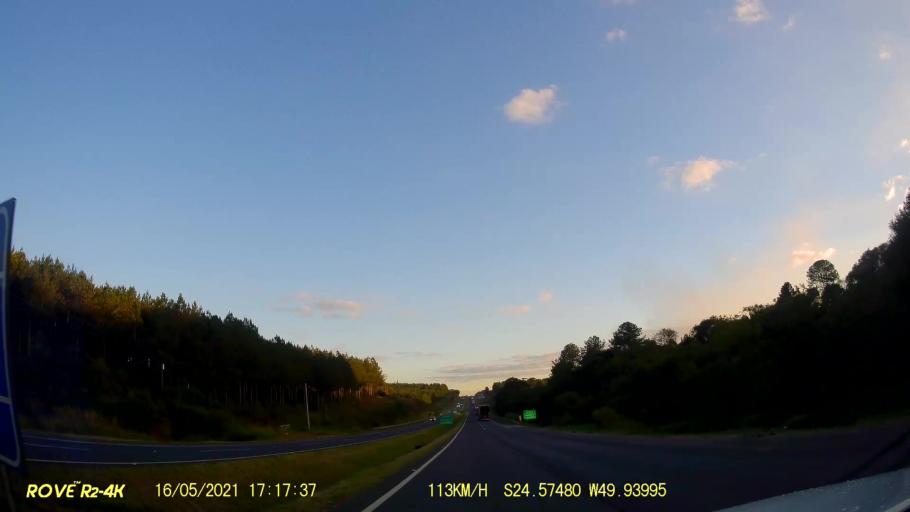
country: BR
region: Parana
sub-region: Pirai Do Sul
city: Pirai do Sul
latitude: -24.5752
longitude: -49.9401
